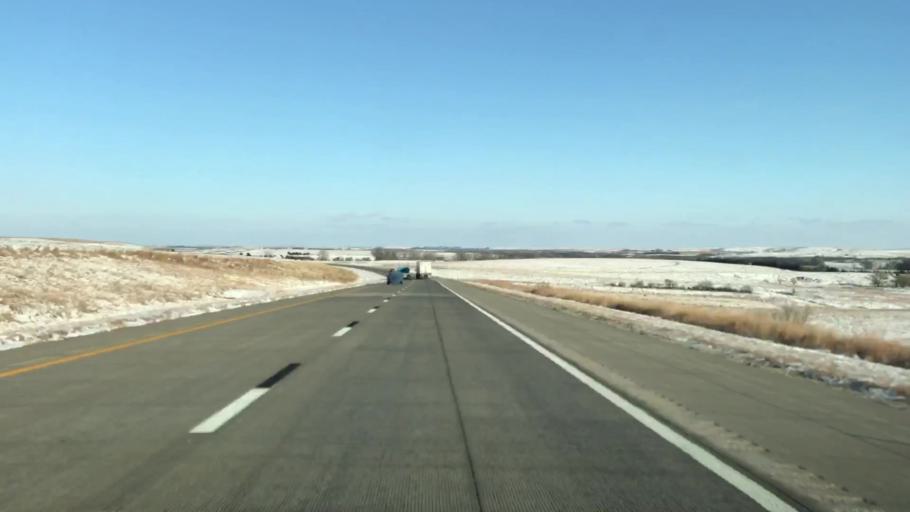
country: US
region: Kansas
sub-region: Lincoln County
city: Lincoln
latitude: 38.8743
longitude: -98.0376
